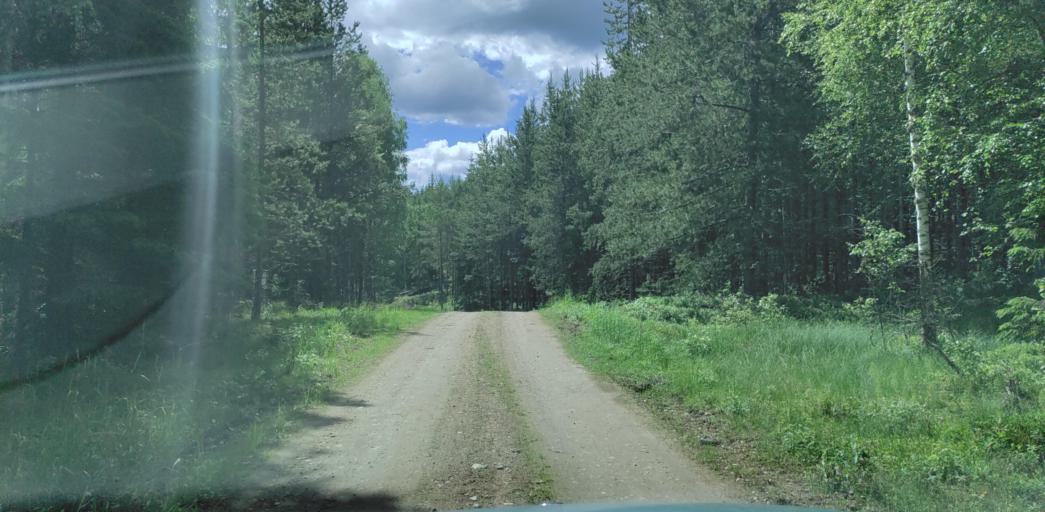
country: SE
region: Vaermland
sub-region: Hagfors Kommun
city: Ekshaerad
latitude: 60.1192
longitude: 13.3265
